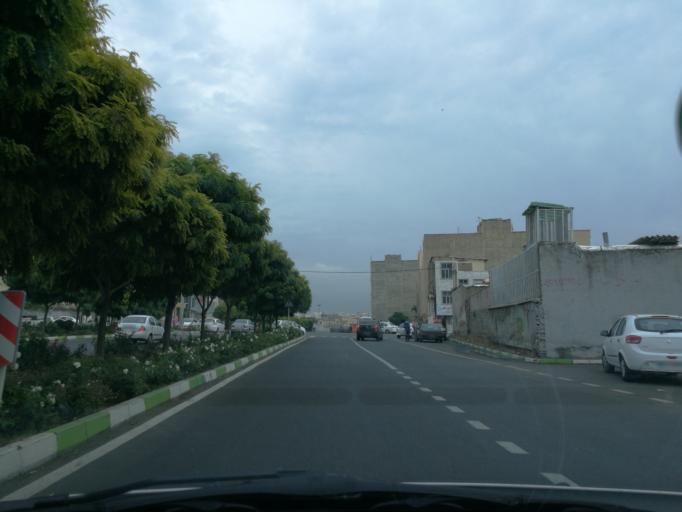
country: IR
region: Alborz
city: Karaj
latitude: 35.8527
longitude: 50.9625
